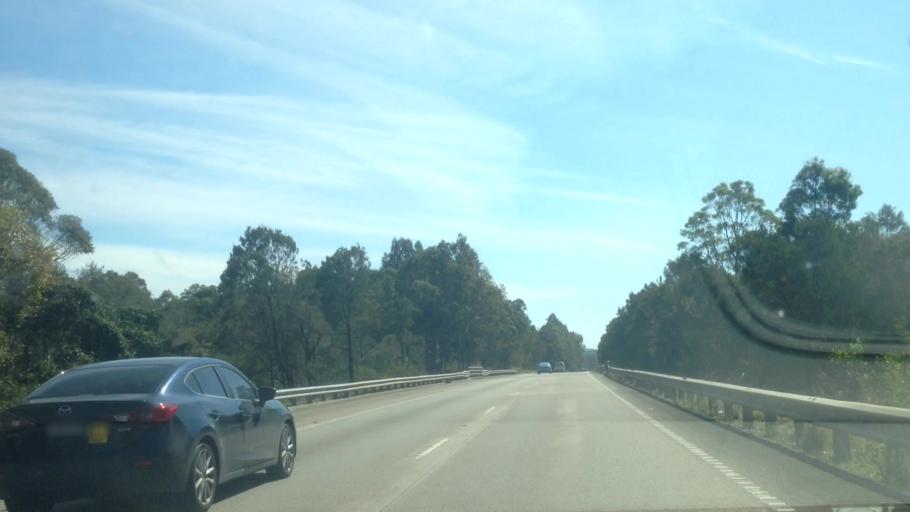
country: AU
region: New South Wales
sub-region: Lake Macquarie Shire
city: Fennell Bay
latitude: -32.9607
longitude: 151.5400
